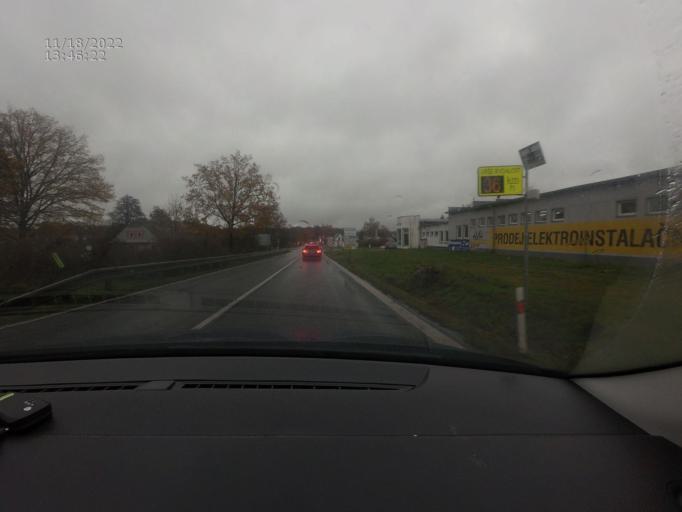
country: CZ
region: Jihocesky
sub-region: Okres Strakonice
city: Blatna
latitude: 49.4253
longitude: 13.8628
